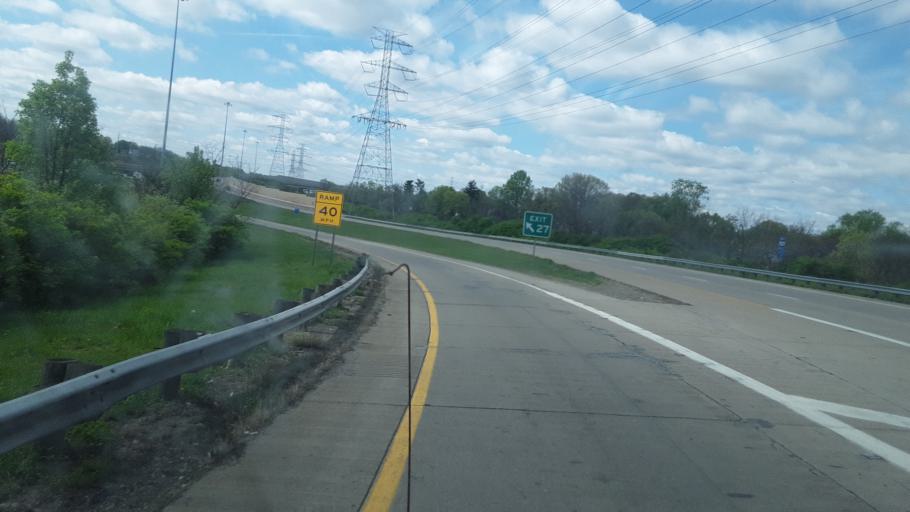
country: US
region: Ohio
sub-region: Hamilton County
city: Lockland
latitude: 39.2101
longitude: -84.4635
